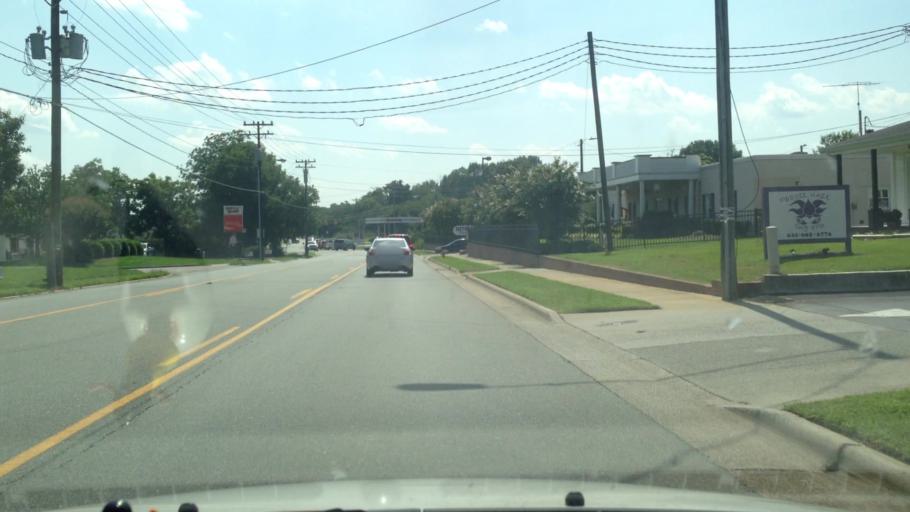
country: US
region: North Carolina
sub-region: Forsyth County
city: Kernersville
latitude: 36.1262
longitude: -80.0683
